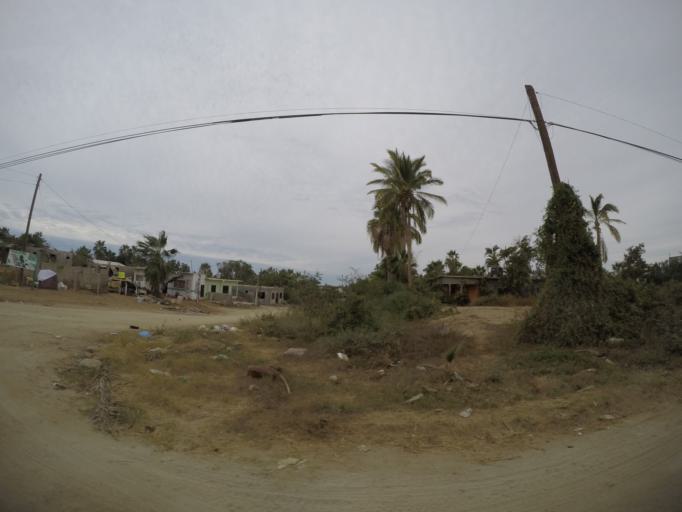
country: MX
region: Baja California Sur
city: Todos Santos
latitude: 23.4418
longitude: -110.2244
